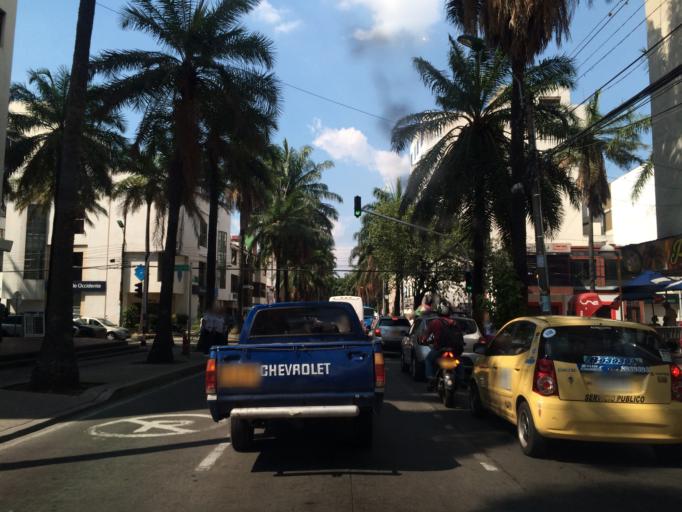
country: CO
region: Valle del Cauca
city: Cali
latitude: 3.4611
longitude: -76.5282
